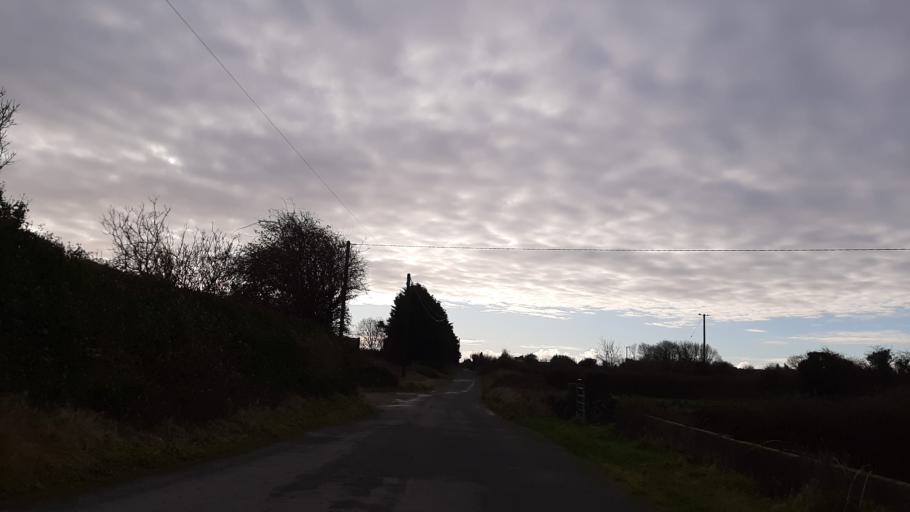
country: IE
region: Connaught
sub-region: County Galway
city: Gaillimh
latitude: 53.3119
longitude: -9.0669
